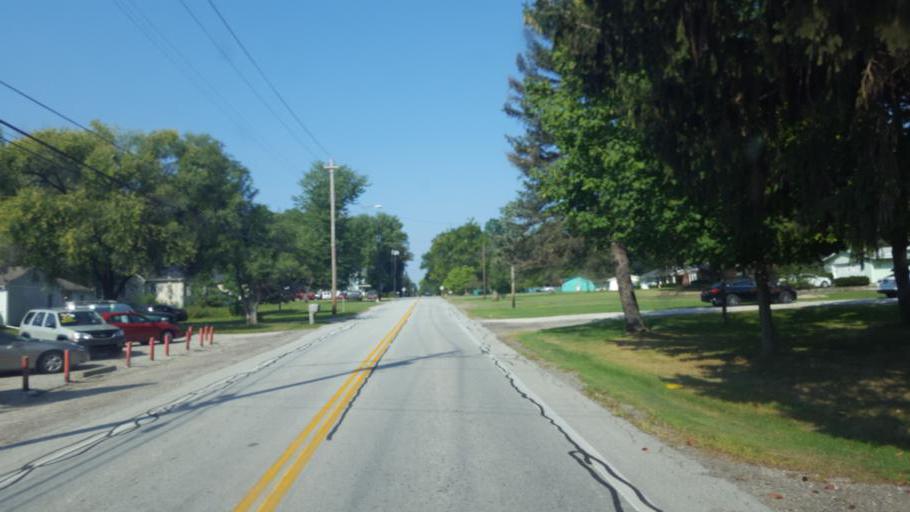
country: US
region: Ohio
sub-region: Ashtabula County
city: Orwell
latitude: 41.6058
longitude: -80.9545
